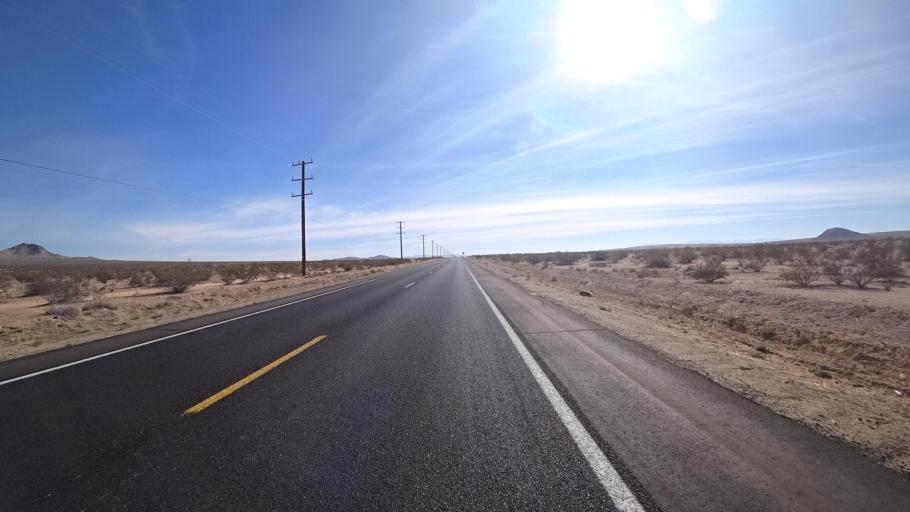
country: US
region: California
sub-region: Kern County
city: California City
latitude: 35.1055
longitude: -117.9221
